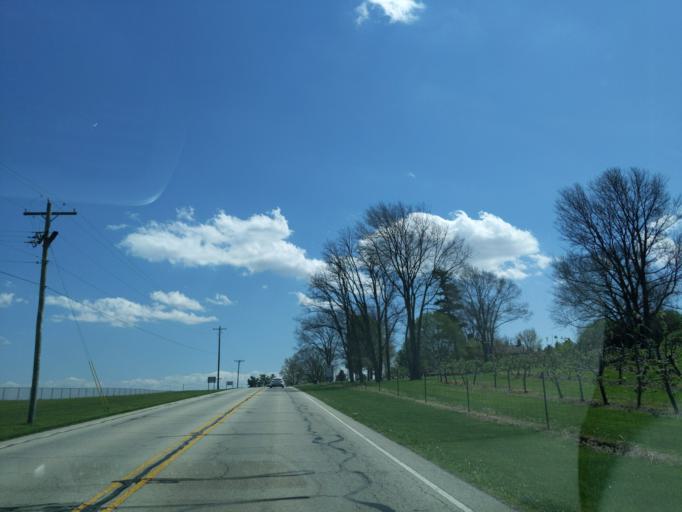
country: US
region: Indiana
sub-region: Decatur County
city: Greensburg
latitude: 39.3851
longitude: -85.5474
